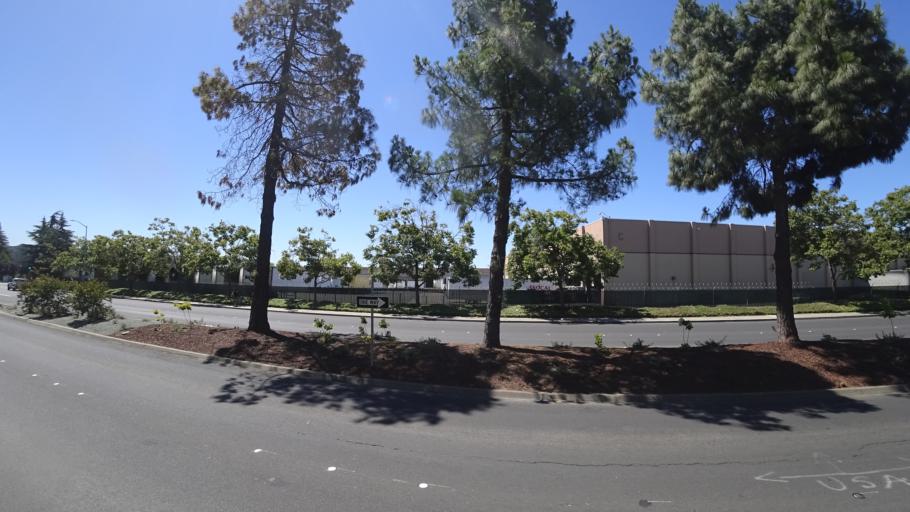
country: US
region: California
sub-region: Alameda County
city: Hayward
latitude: 37.6180
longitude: -122.0859
